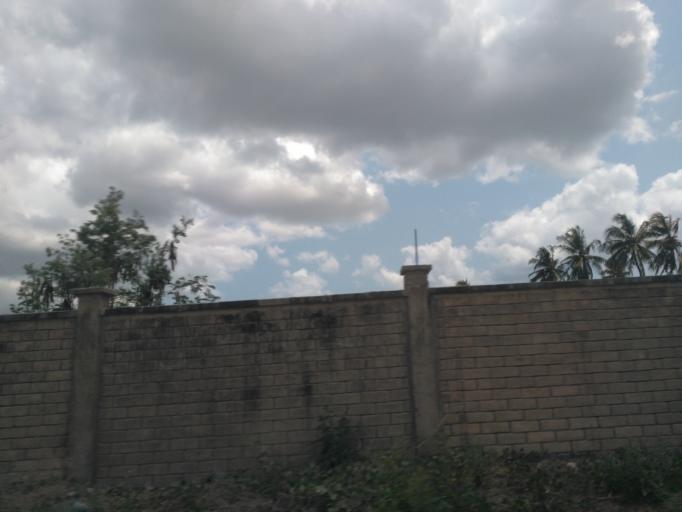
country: TZ
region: Dar es Salaam
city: Dar es Salaam
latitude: -6.8778
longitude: 39.3435
